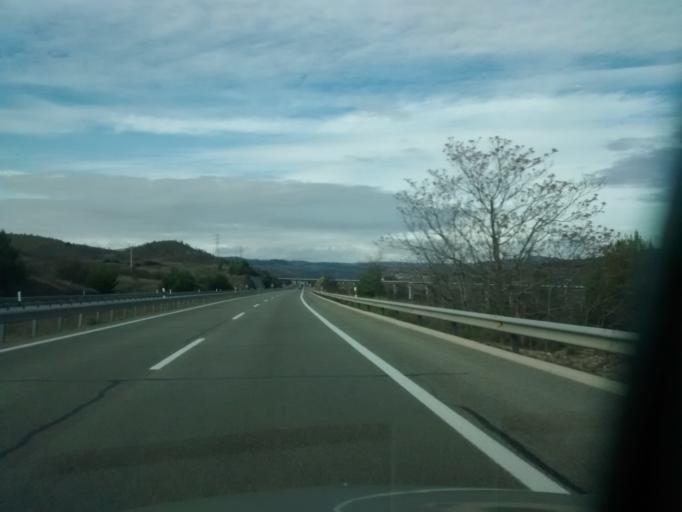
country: ES
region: Aragon
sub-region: Provincia de Zaragoza
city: Valtorres
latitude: 41.3100
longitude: -1.7621
